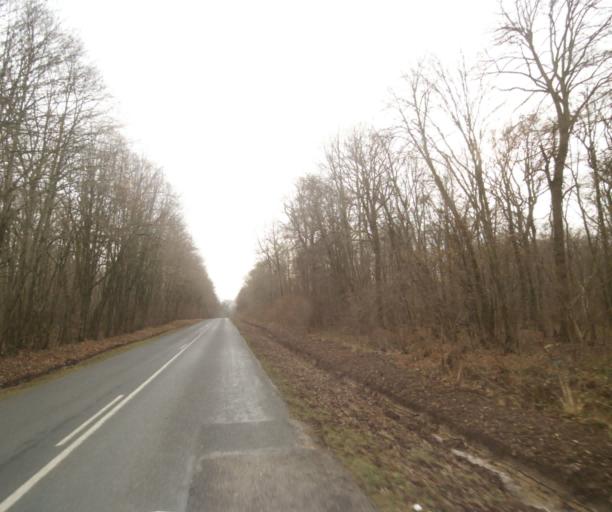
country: FR
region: Champagne-Ardenne
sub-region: Departement de la Haute-Marne
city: Villiers-en-Lieu
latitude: 48.7111
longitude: 4.8873
